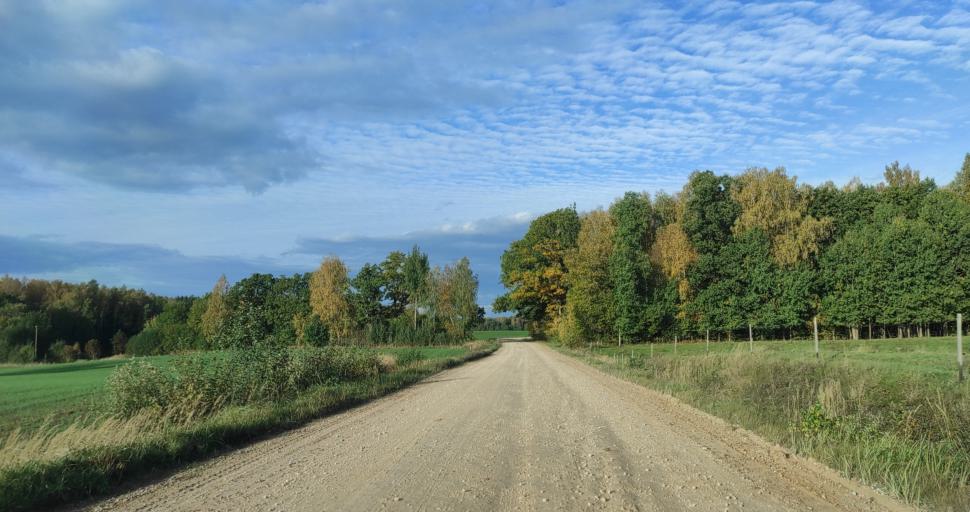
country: LV
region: Skrunda
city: Skrunda
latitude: 56.7433
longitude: 21.8454
